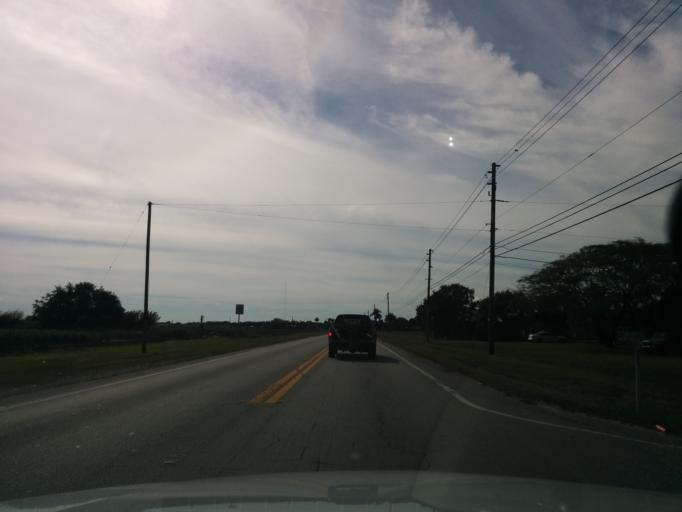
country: US
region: Florida
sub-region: Miami-Dade County
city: Richmond West
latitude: 25.6030
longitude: -80.4788
